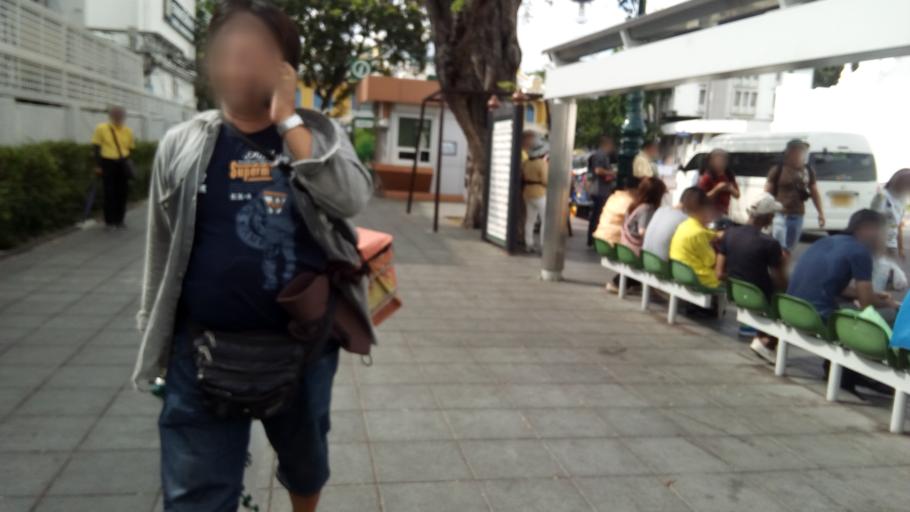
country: TH
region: Bangkok
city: Bangkok
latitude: 13.7518
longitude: 100.4893
